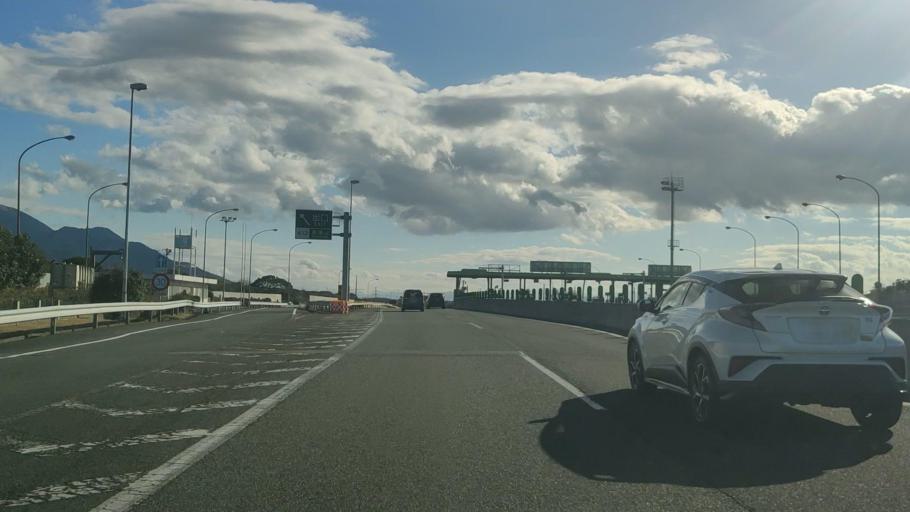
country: JP
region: Fukuoka
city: Nakama
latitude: 33.7970
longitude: 130.7436
